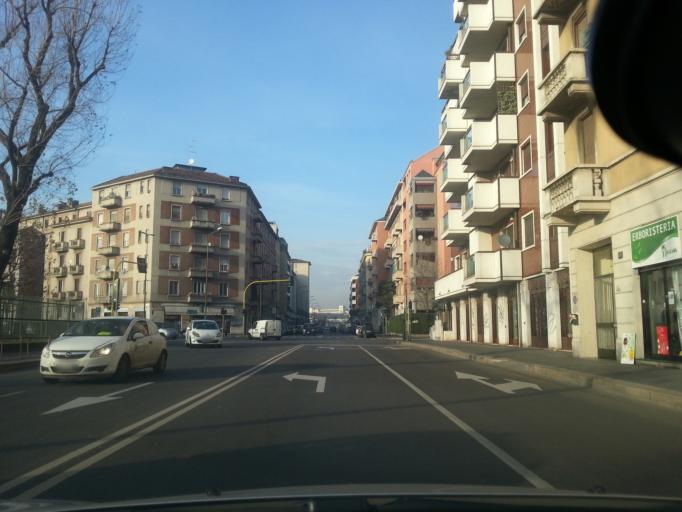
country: IT
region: Lombardy
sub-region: Citta metropolitana di Milano
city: Milano
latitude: 45.5005
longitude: 9.1904
